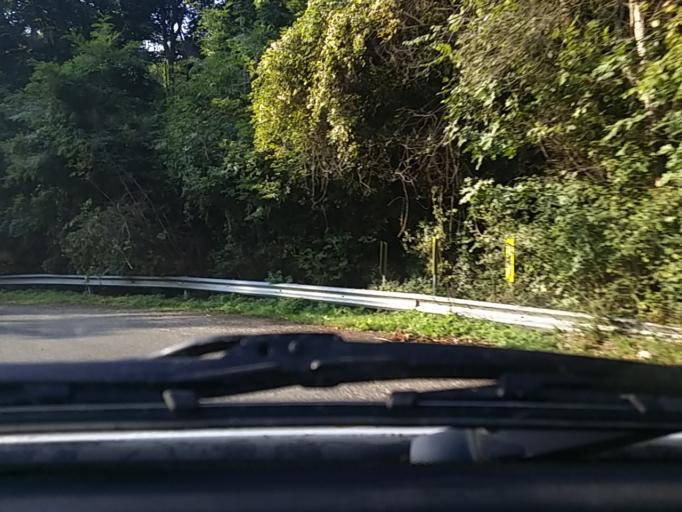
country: HU
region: Pest
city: Nagykovacsi
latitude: 47.7078
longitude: 19.0141
